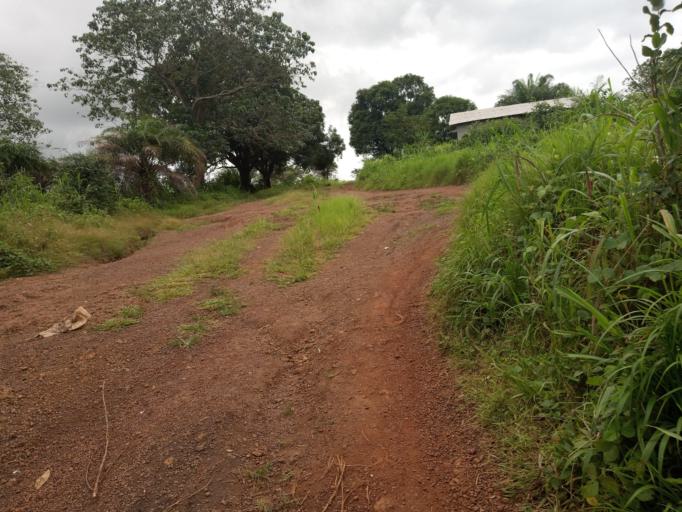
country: SL
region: Northern Province
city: Kamakwie
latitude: 9.4890
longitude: -12.2455
